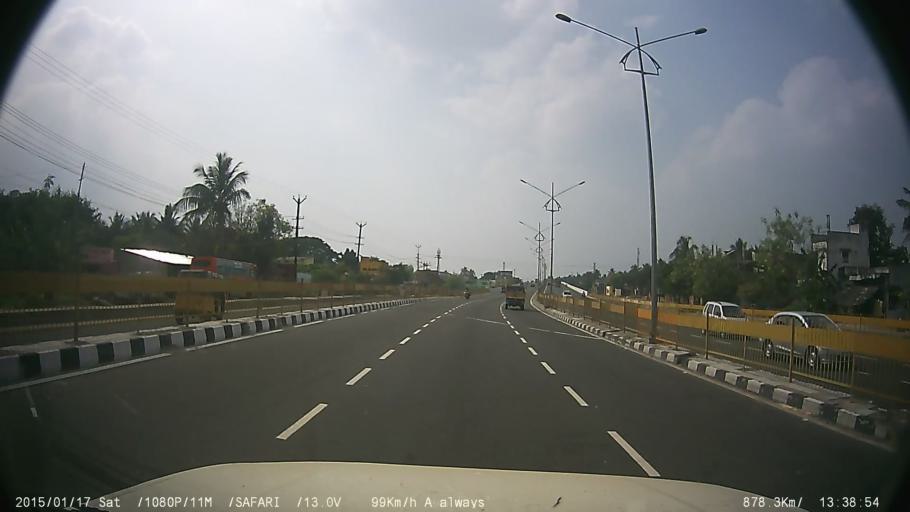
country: IN
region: Tamil Nadu
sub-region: Vellore
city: Katpadi
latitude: 12.9423
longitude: 79.1905
